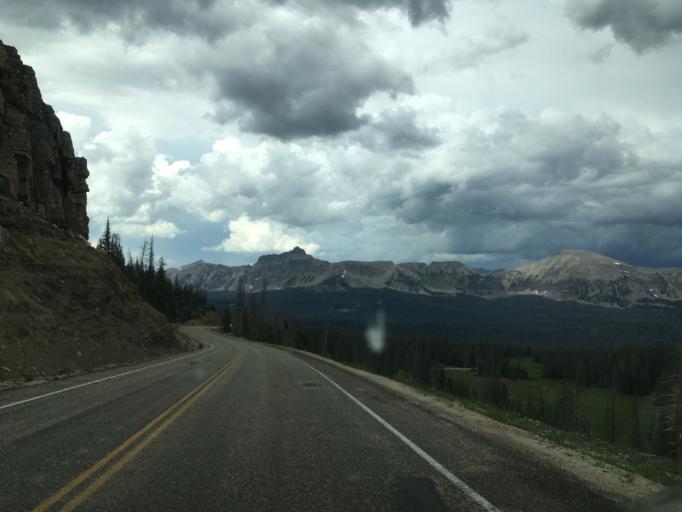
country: US
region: Utah
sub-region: Summit County
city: Kamas
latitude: 40.6870
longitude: -110.9002
